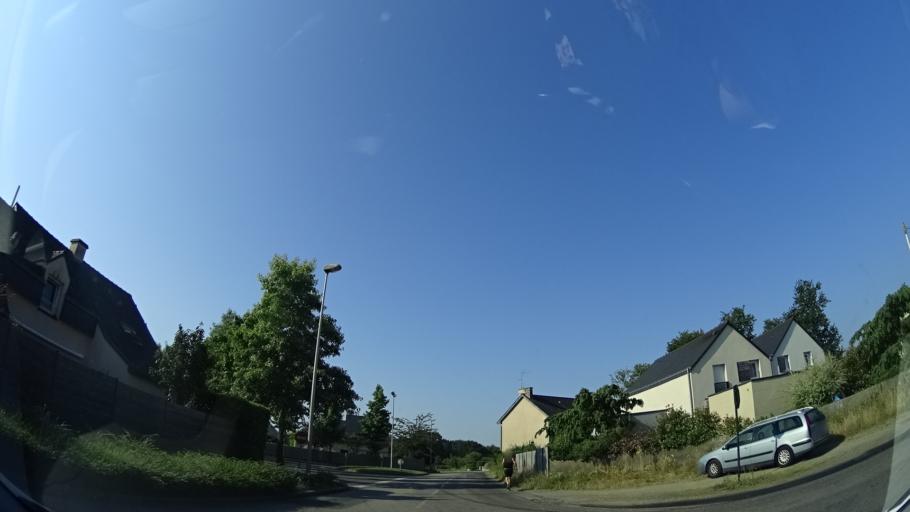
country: FR
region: Brittany
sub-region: Departement d'Ille-et-Vilaine
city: Pace
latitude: 48.1536
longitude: -1.7923
